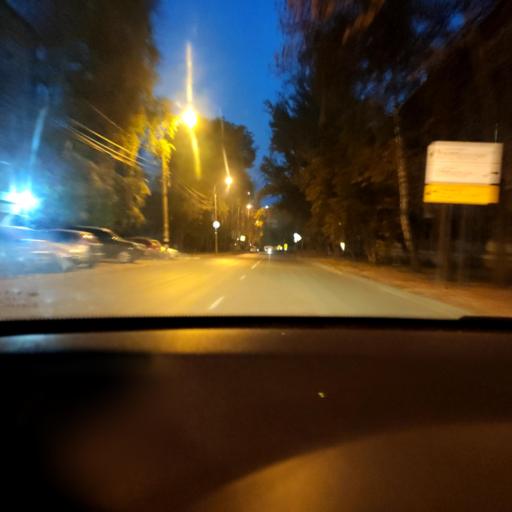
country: RU
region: Samara
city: Samara
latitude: 53.2025
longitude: 50.1741
